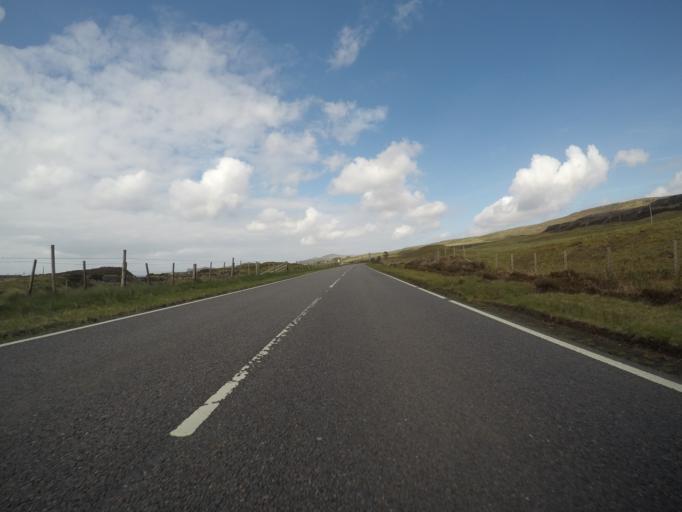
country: GB
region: Scotland
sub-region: Highland
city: Portree
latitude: 57.5534
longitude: -6.3657
